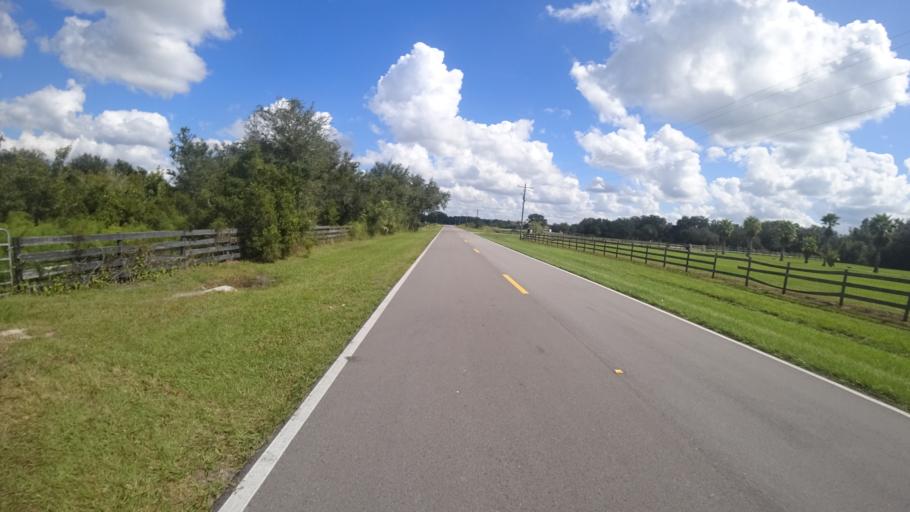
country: US
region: Florida
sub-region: Sarasota County
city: Lake Sarasota
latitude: 27.2889
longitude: -82.2245
